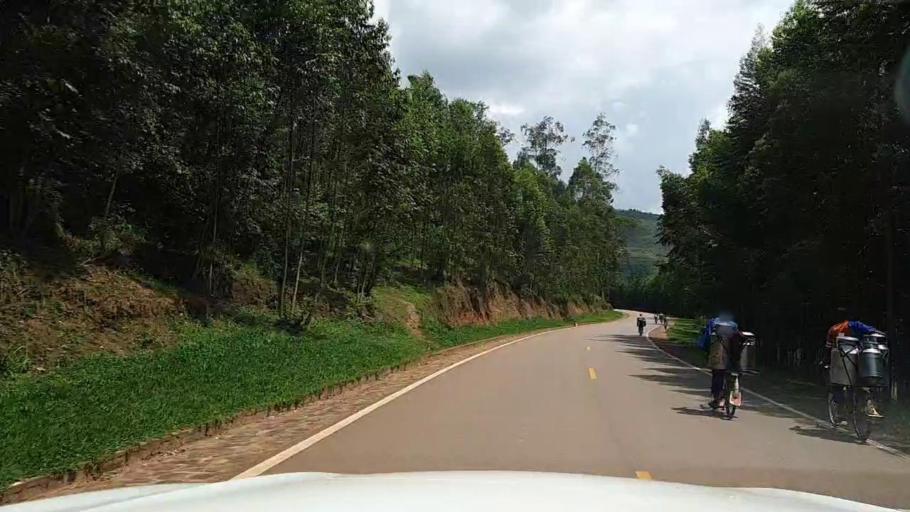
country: RW
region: Kigali
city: Kigali
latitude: -1.8160
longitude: 30.0935
